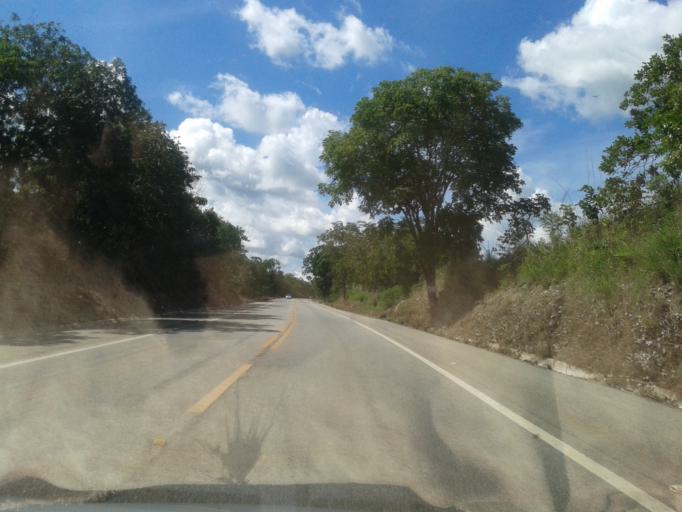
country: BR
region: Goias
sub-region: Itapuranga
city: Itapuranga
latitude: -15.6326
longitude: -50.2303
